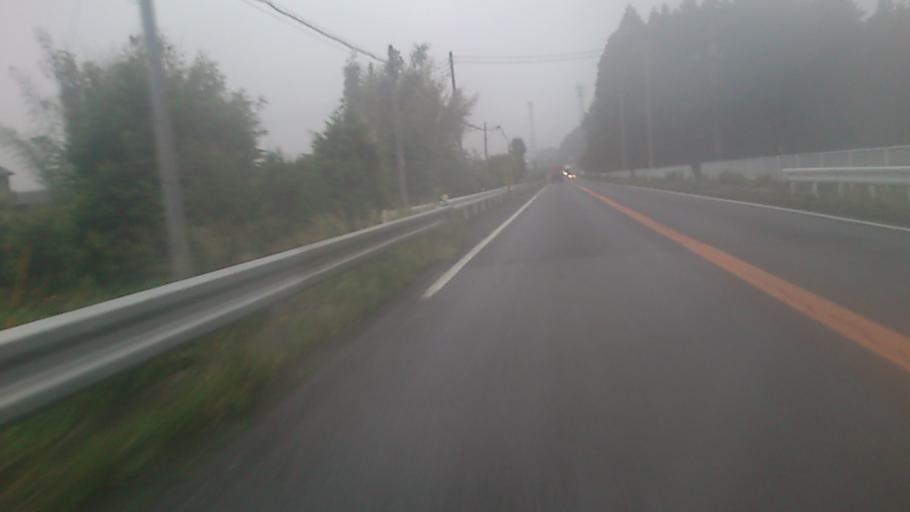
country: JP
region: Tochigi
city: Kuroiso
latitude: 37.0342
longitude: 140.0946
